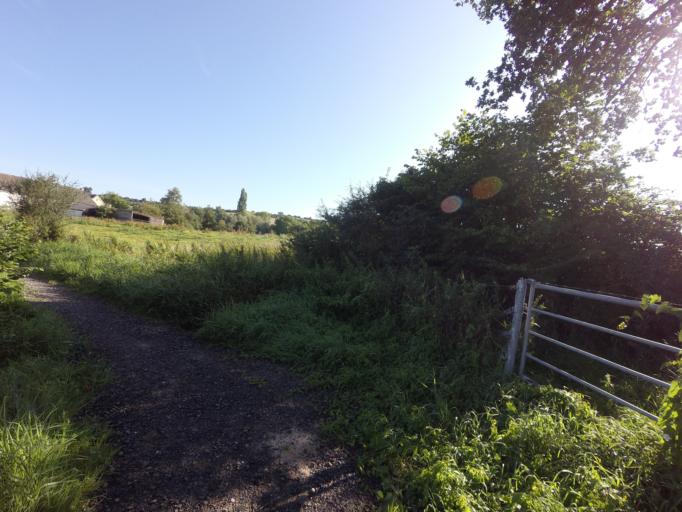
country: NL
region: Limburg
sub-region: Gemeente Vaals
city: Vaals
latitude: 50.7849
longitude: 5.9982
